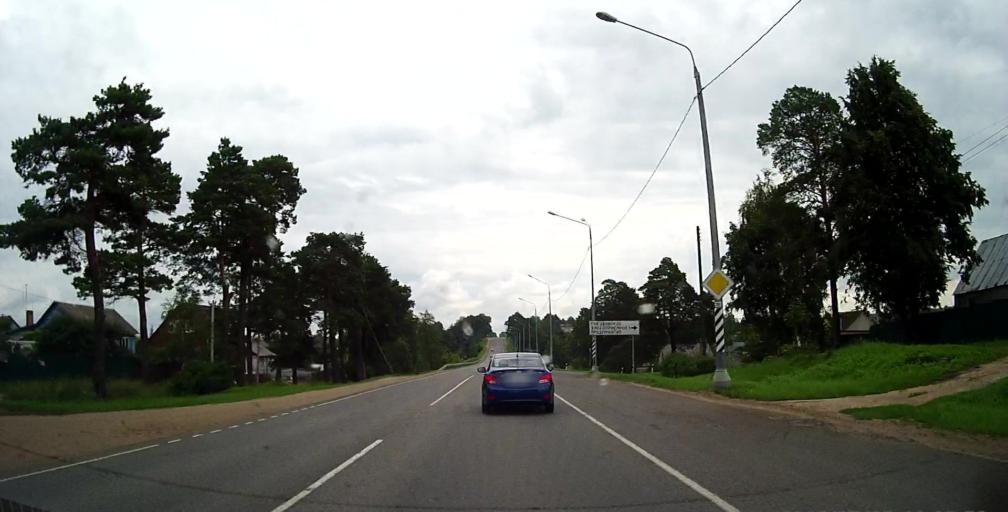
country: RU
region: Smolensk
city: Katyn'
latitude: 54.7845
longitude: 31.8498
